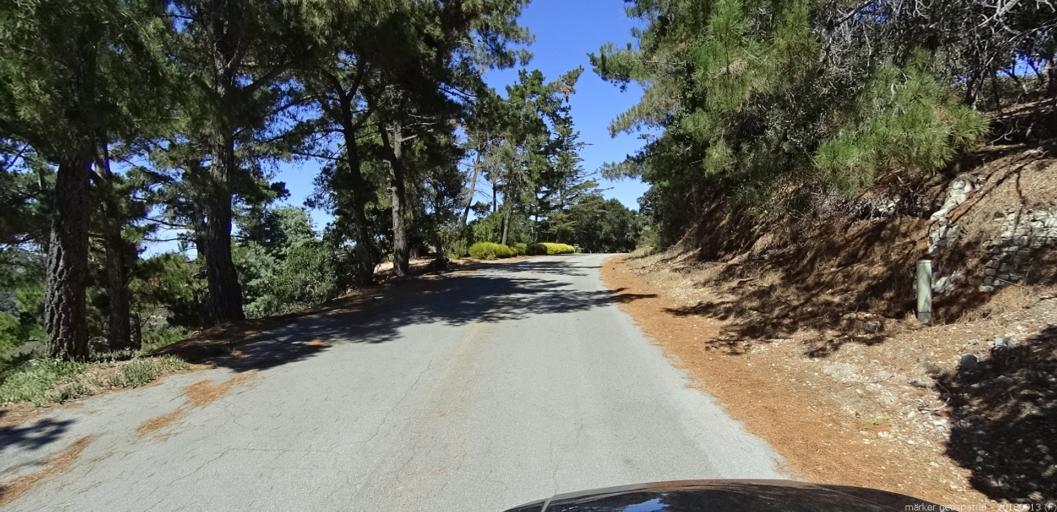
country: US
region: California
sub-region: Monterey County
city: Carmel Valley Village
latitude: 36.5435
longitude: -121.7963
